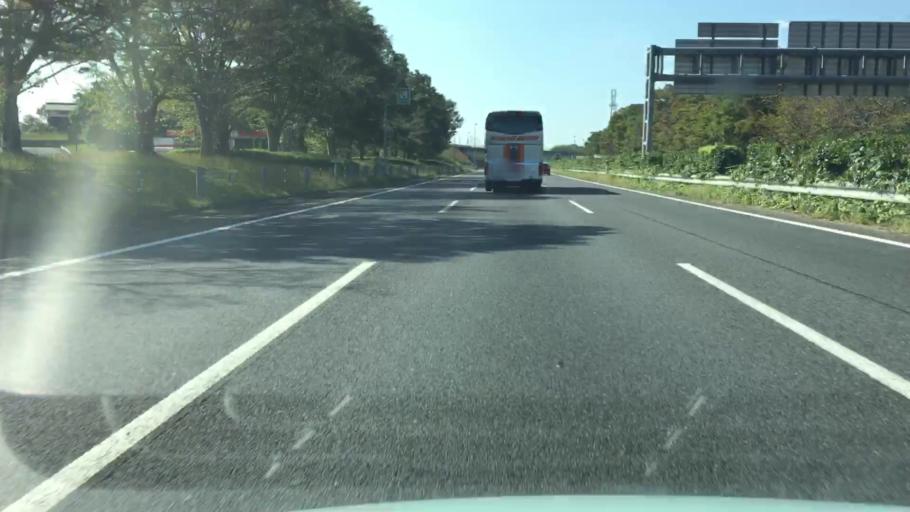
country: JP
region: Ibaraki
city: Tomobe
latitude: 36.3104
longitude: 140.3416
